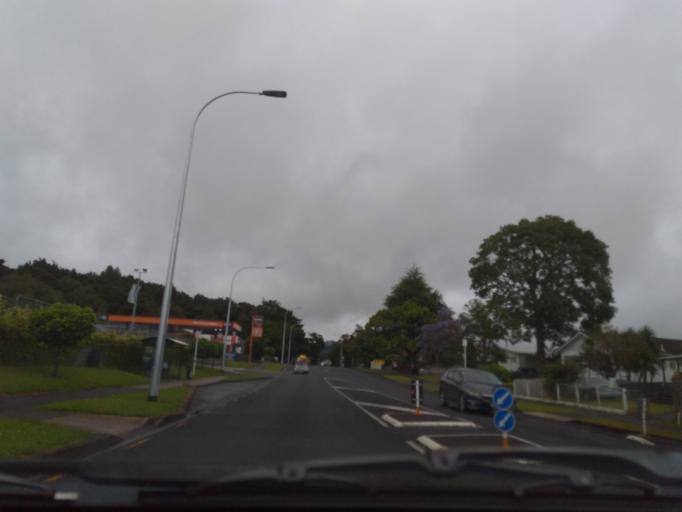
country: NZ
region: Northland
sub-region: Whangarei
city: Whangarei
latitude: -35.6828
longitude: 174.3220
